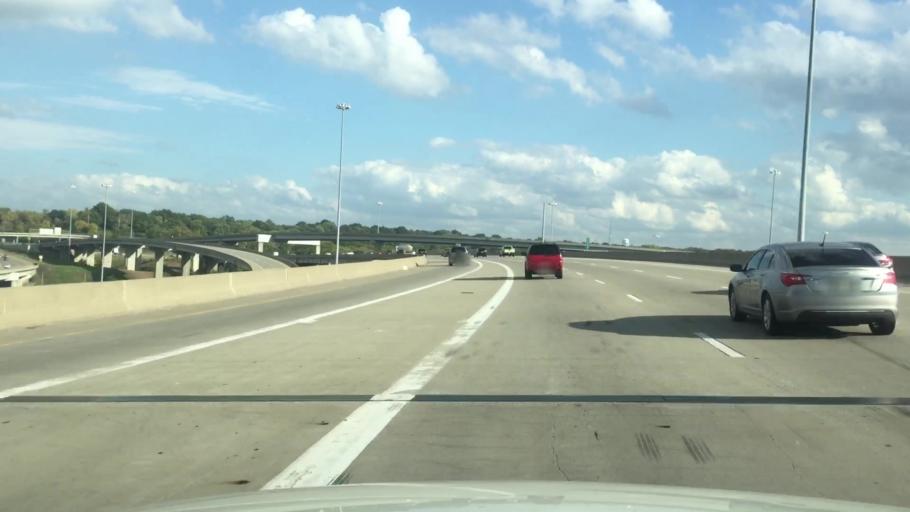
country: US
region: Missouri
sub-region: Jackson County
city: Grandview
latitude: 38.9340
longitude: -94.5311
